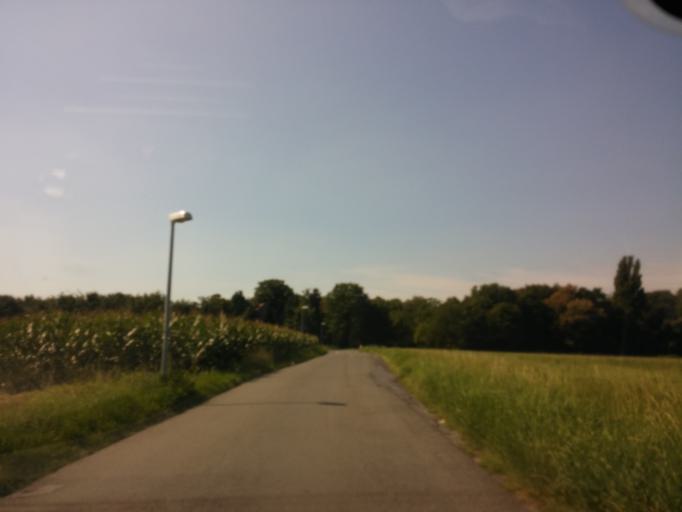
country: DE
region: North Rhine-Westphalia
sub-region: Regierungsbezirk Munster
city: Gladbeck
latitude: 51.5572
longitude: 7.0551
